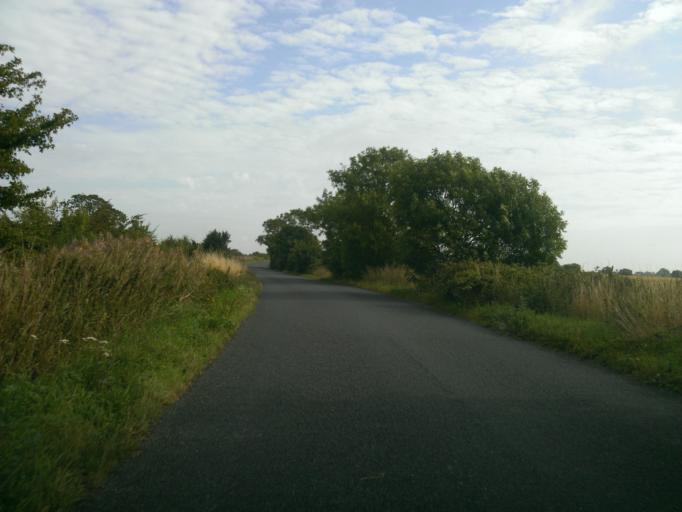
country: GB
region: England
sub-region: Essex
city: Saint Osyth
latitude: 51.8111
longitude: 1.0913
